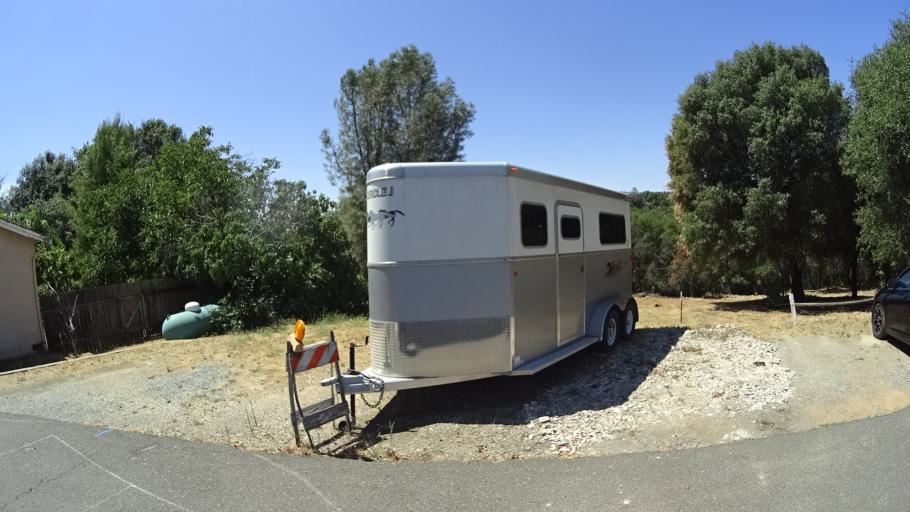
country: US
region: California
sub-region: Calaveras County
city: Angels Camp
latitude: 38.0681
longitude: -120.5438
